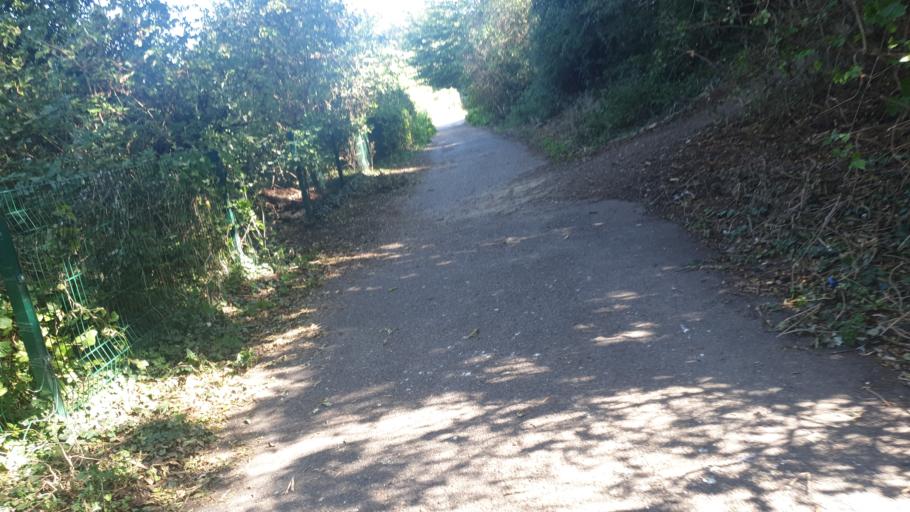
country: GB
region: England
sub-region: Essex
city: Dovercourt
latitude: 51.9388
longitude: 1.2669
